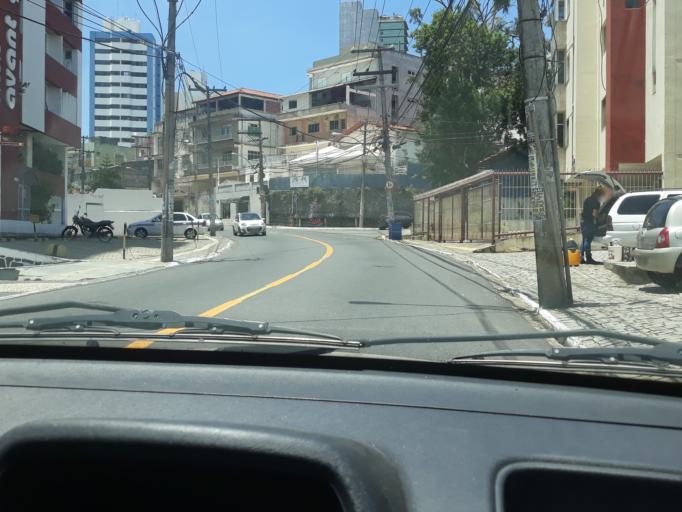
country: BR
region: Bahia
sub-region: Salvador
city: Salvador
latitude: -12.9994
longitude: -38.5037
